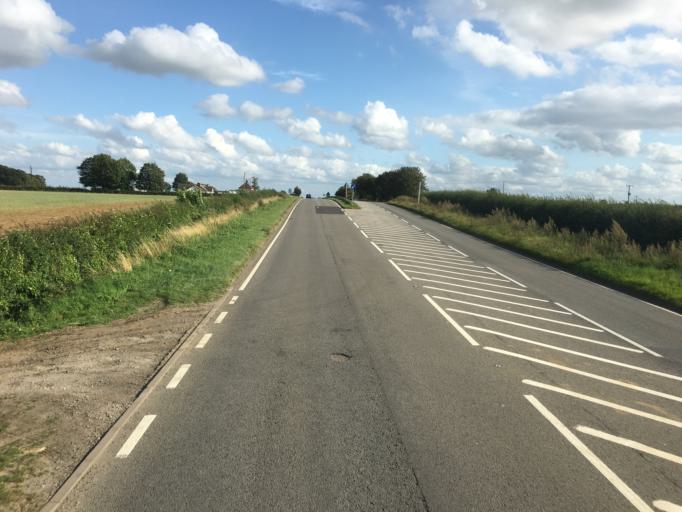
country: GB
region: England
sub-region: Leicestershire
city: Lutterworth
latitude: 52.4469
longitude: -1.2491
